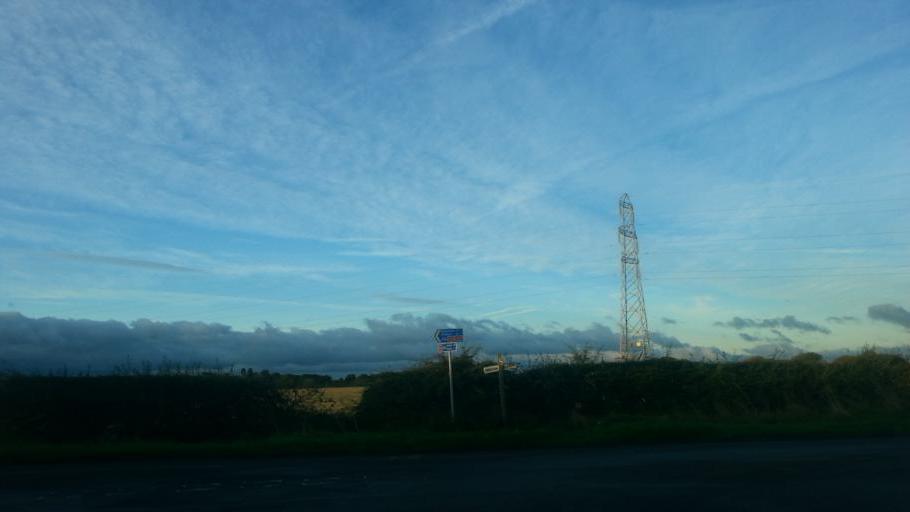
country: GB
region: England
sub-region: Nottinghamshire
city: Farndon
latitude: 53.0032
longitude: -0.8299
